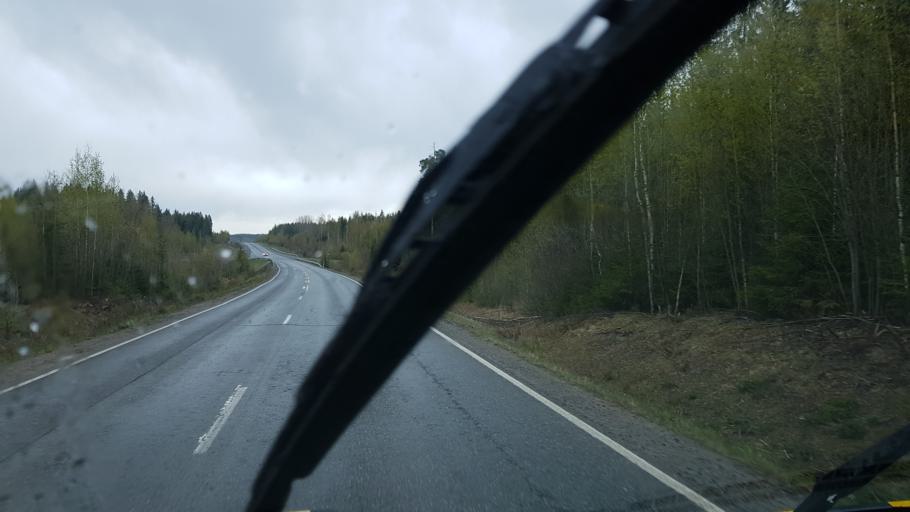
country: FI
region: Pirkanmaa
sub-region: Tampere
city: Pirkkala
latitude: 61.4072
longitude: 23.6335
